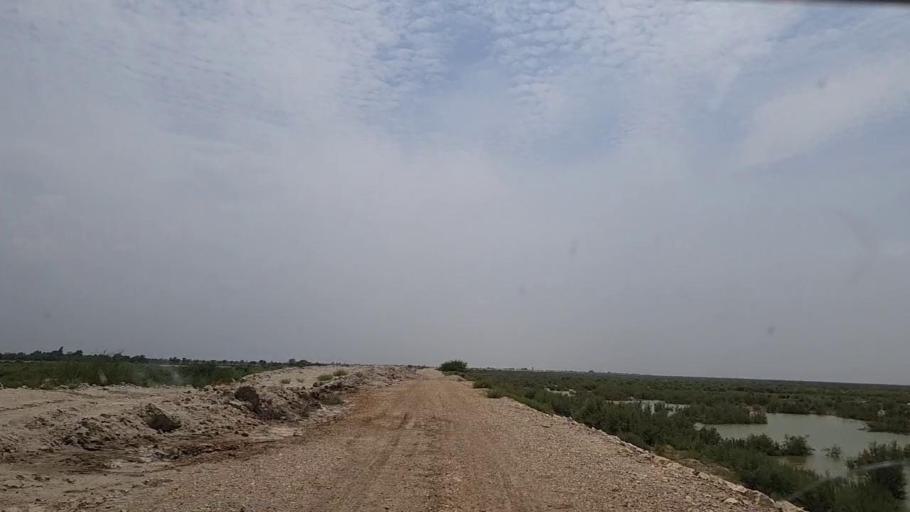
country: PK
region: Sindh
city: Phulji
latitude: 26.8744
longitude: 67.6506
